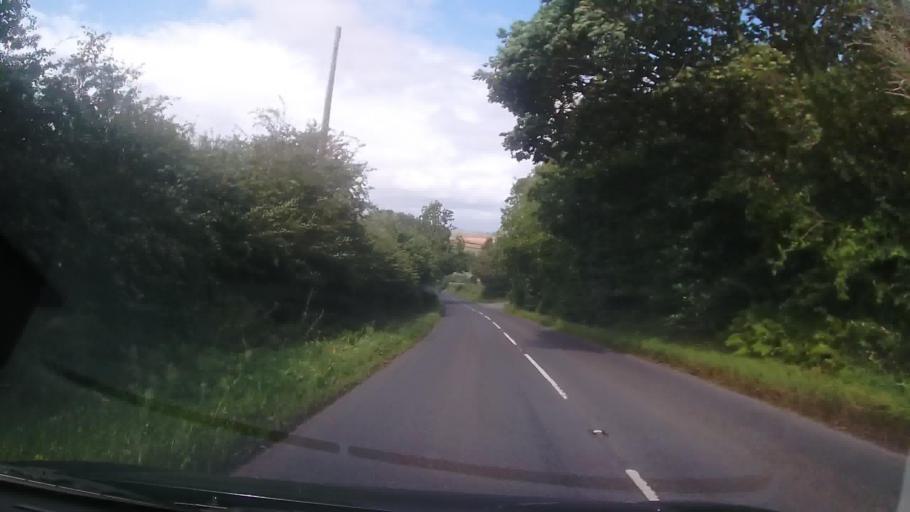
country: GB
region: England
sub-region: Shropshire
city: Acton
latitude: 52.4504
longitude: -3.0263
